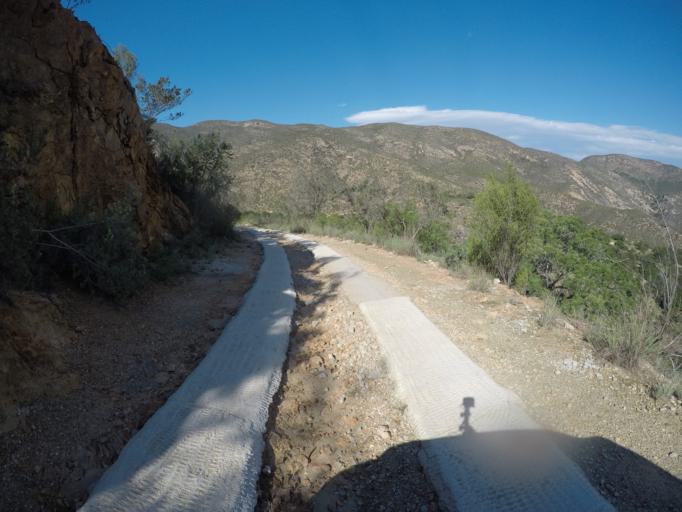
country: ZA
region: Eastern Cape
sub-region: Cacadu District Municipality
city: Kareedouw
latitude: -33.6441
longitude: 24.4620
